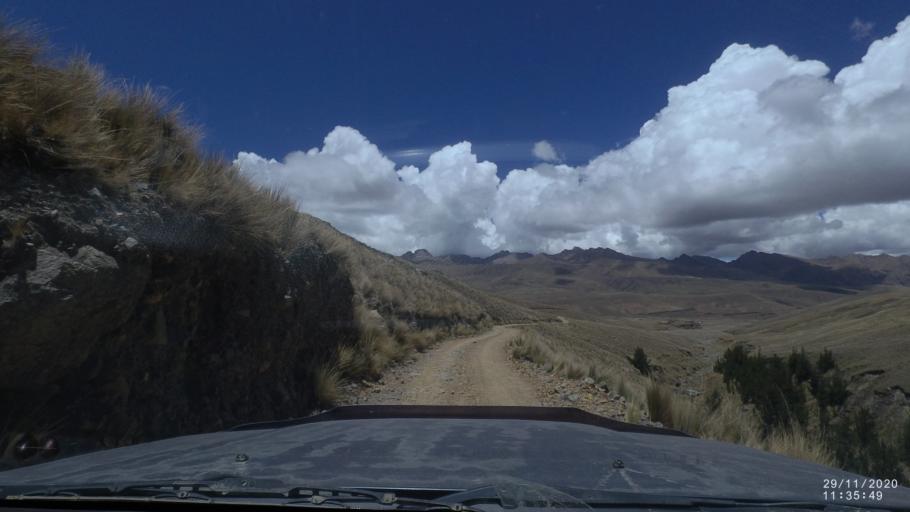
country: BO
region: Cochabamba
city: Cochabamba
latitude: -17.1943
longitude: -66.2251
